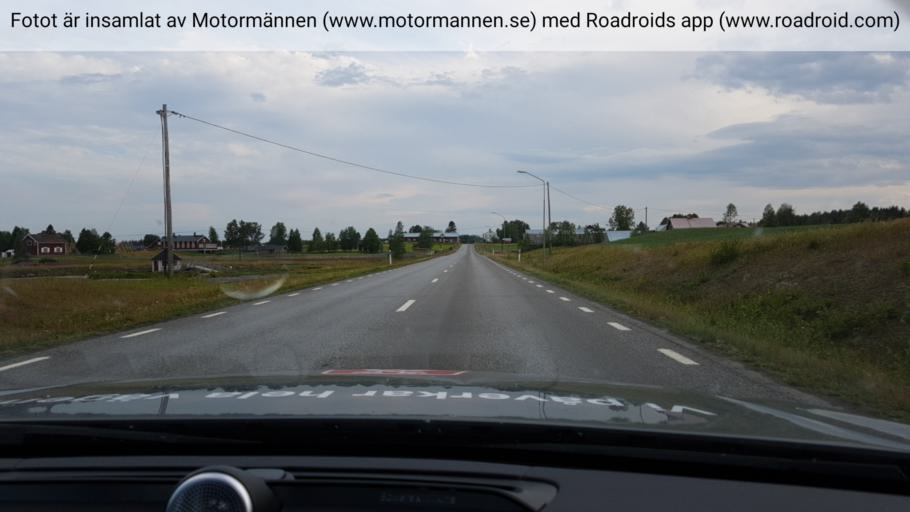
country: SE
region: Jaemtland
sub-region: Stroemsunds Kommun
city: Stroemsund
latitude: 63.5017
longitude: 15.2612
